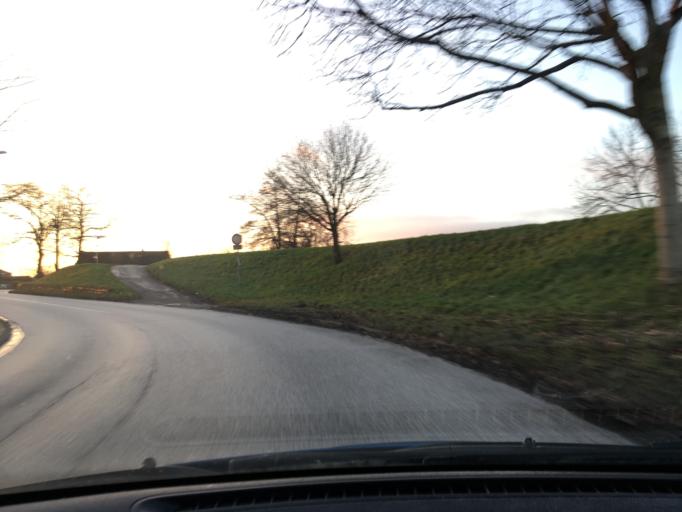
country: DE
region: Hamburg
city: Altona
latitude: 53.5094
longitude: 9.8744
